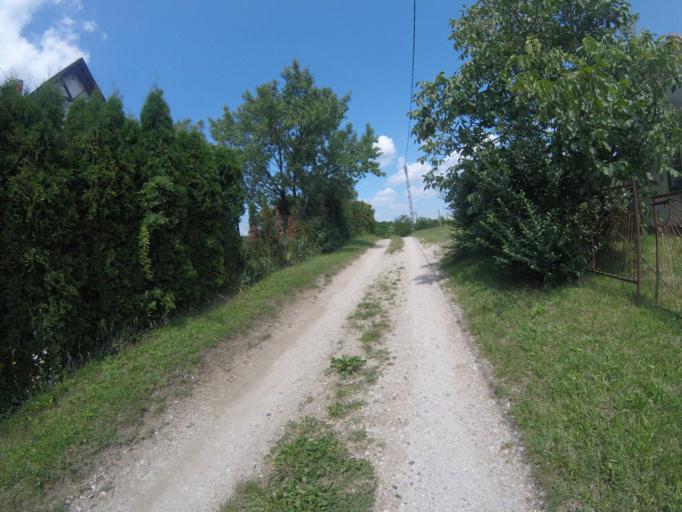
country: HU
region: Zala
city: Nagykanizsa
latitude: 46.5544
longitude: 17.0342
